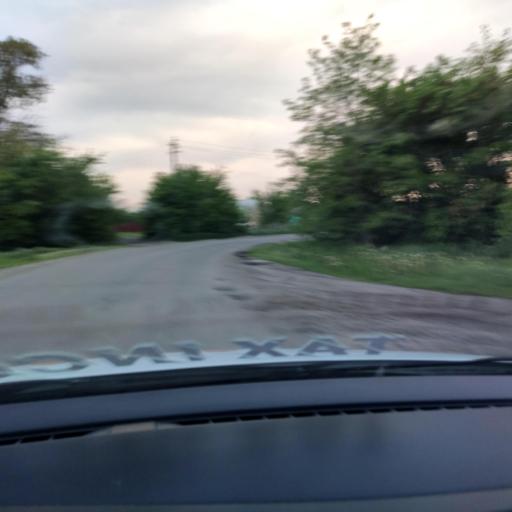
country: RU
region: Voronezj
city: Maslovka
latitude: 51.4569
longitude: 39.2343
